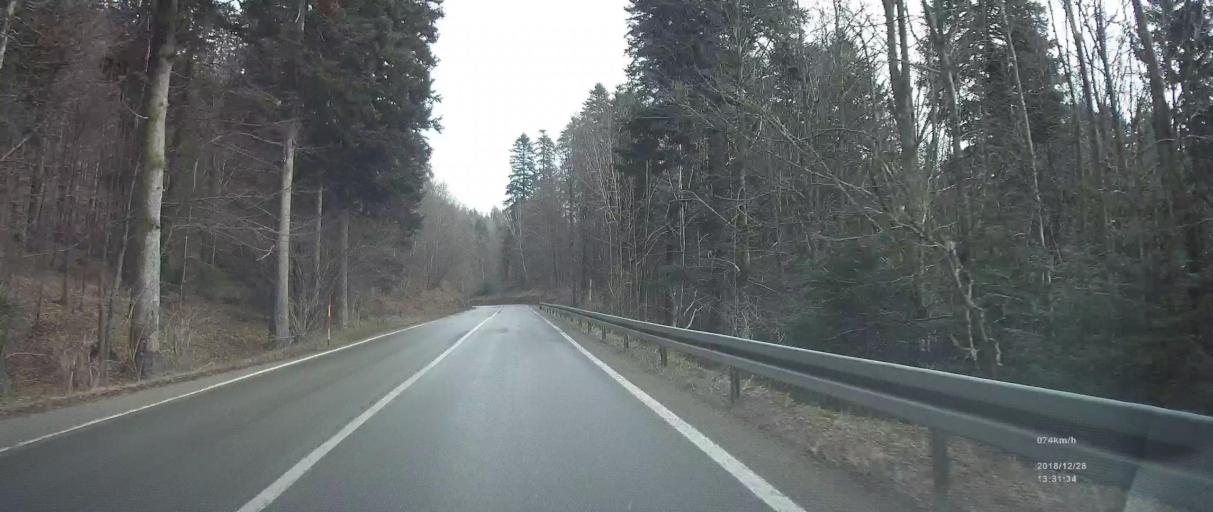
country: HR
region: Primorsko-Goranska
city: Hreljin
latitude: 45.3493
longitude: 14.6527
